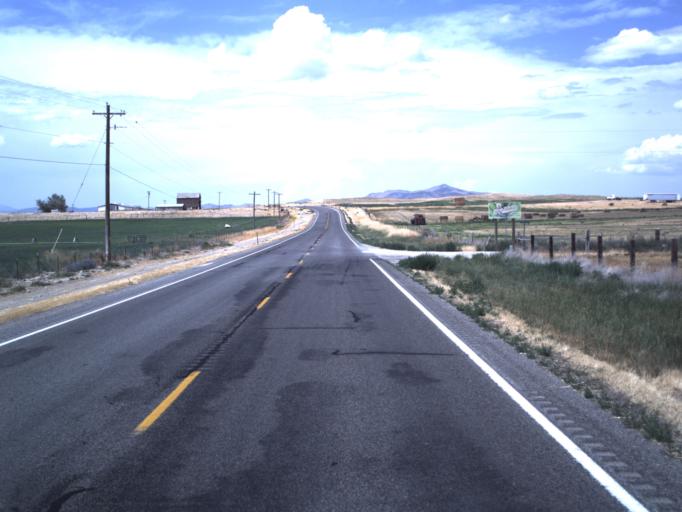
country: US
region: Utah
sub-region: Sanpete County
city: Moroni
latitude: 39.4901
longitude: -111.5631
